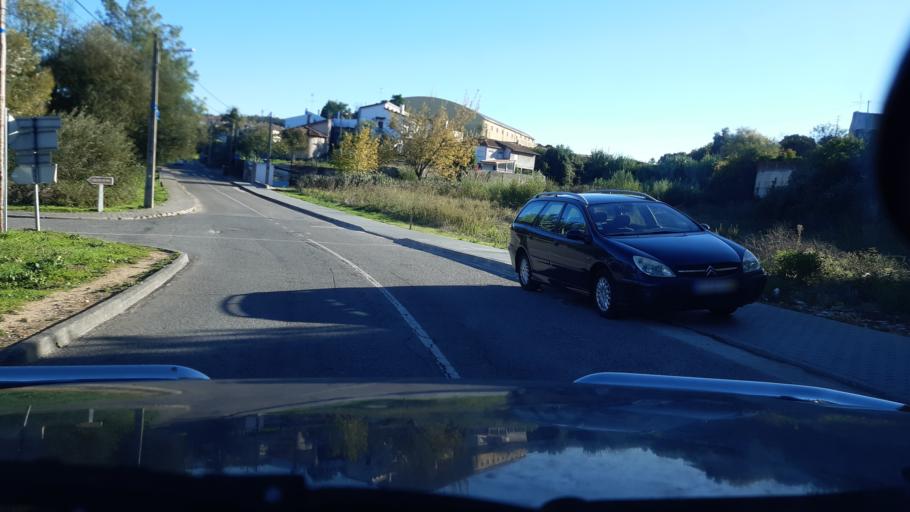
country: PT
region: Aveiro
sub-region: Agueda
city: Agueda
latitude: 40.5599
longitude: -8.4416
